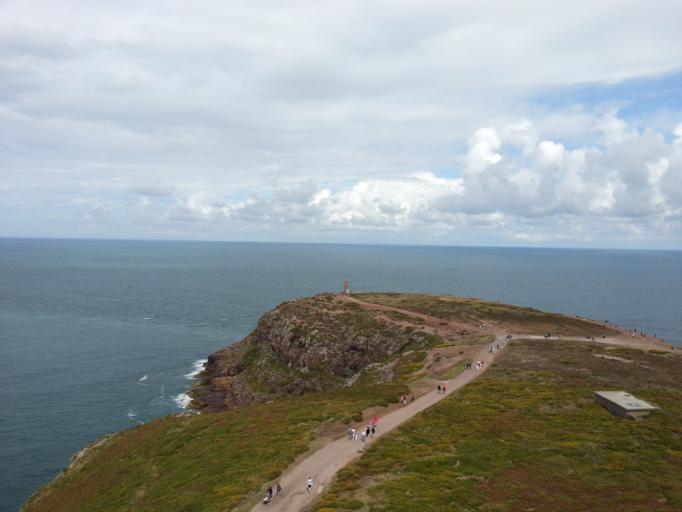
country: FR
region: Brittany
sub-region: Departement des Cotes-d'Armor
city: Saint-Cast-le-Guildo
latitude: 48.6841
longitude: -2.3189
